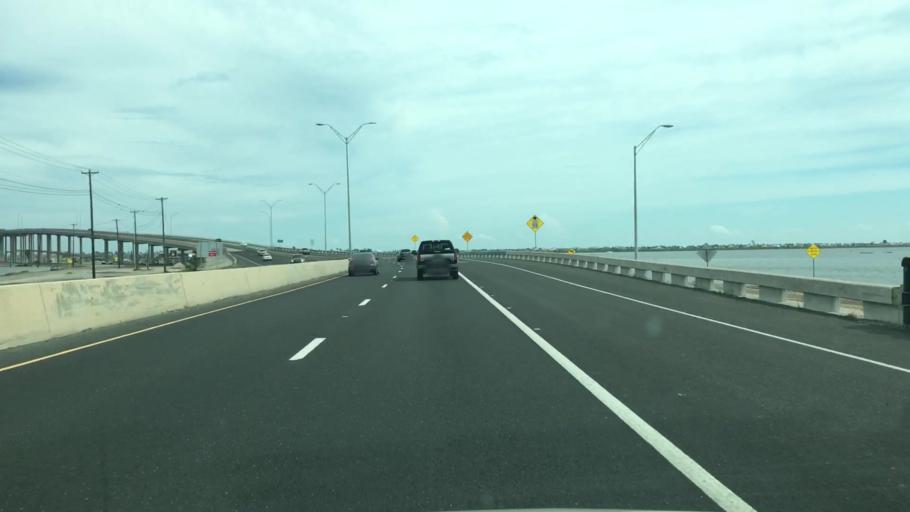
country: US
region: Texas
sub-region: Nueces County
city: Corpus Christi
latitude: 27.6390
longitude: -97.2463
